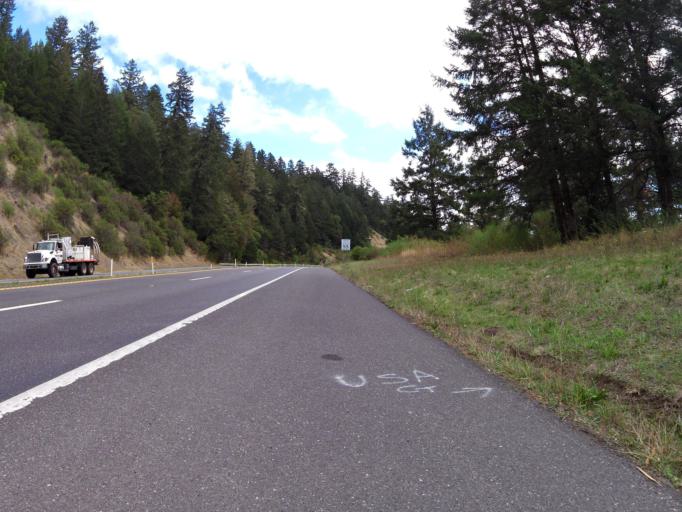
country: US
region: California
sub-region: Humboldt County
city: Redway
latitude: 40.0932
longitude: -123.7927
